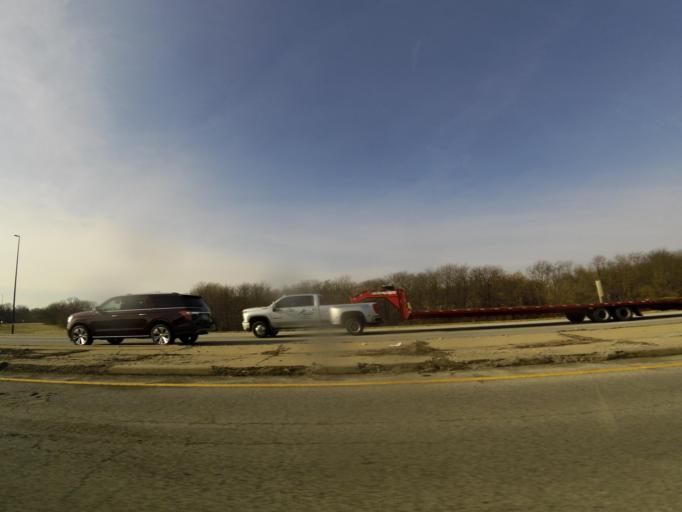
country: US
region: Illinois
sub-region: Macon County
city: Forsyth
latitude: 39.9115
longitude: -88.9552
